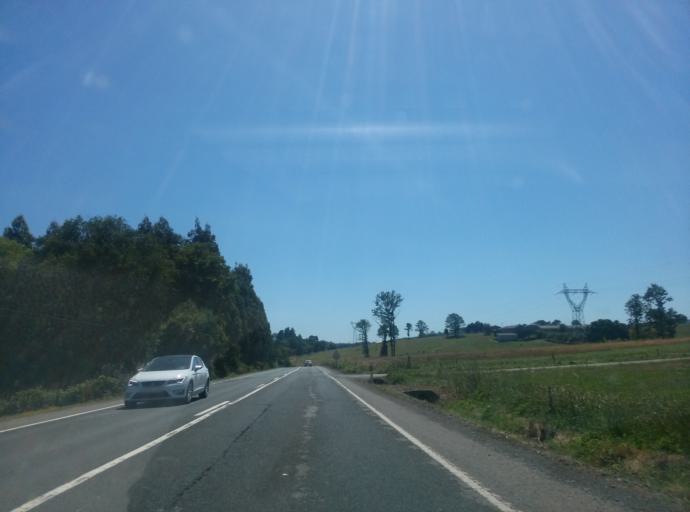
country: ES
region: Galicia
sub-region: Provincia de Lugo
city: Pol
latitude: 43.1744
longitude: -7.3607
